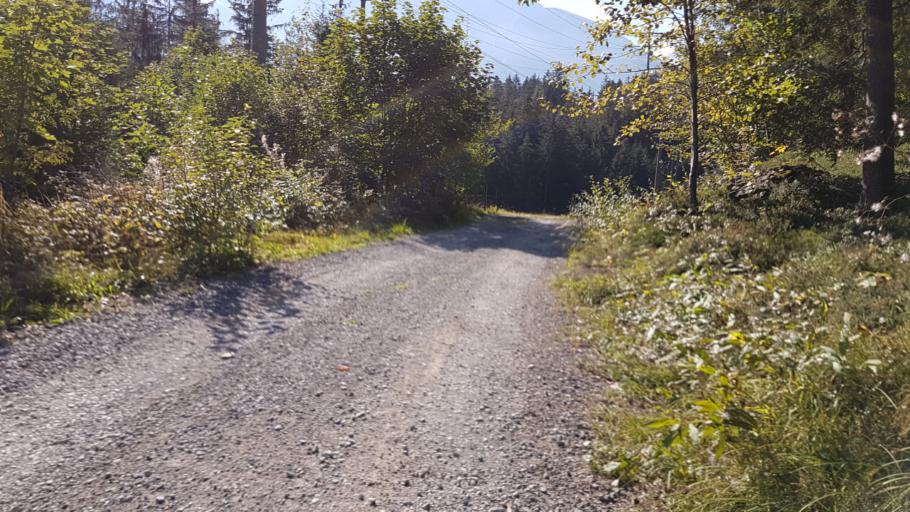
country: CH
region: Bern
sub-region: Frutigen-Niedersimmental District
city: Kandersteg
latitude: 46.5105
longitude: 7.6714
